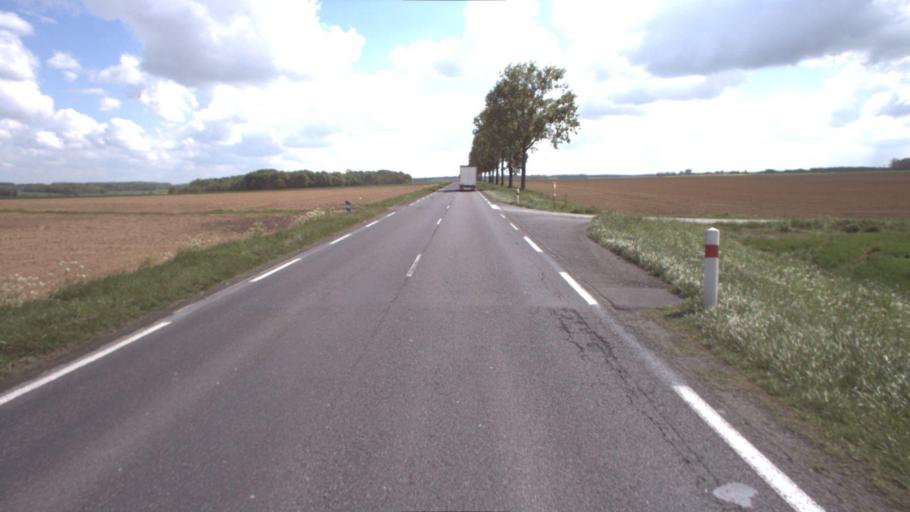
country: FR
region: Ile-de-France
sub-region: Departement de Seine-et-Marne
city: Choisy-en-Brie
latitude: 48.6926
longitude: 3.2026
